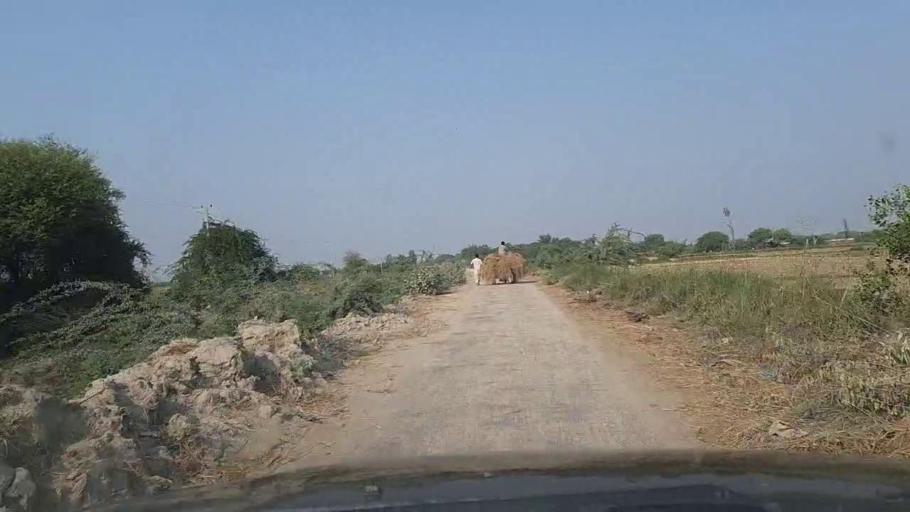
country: PK
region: Sindh
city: Mirpur Batoro
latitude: 24.7100
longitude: 68.2544
